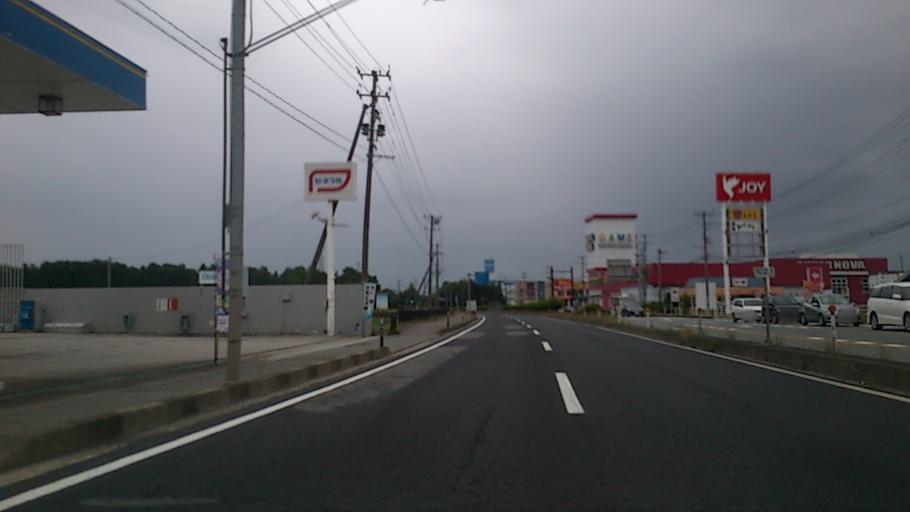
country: JP
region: Yamagata
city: Tendo
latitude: 38.3439
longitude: 140.3761
